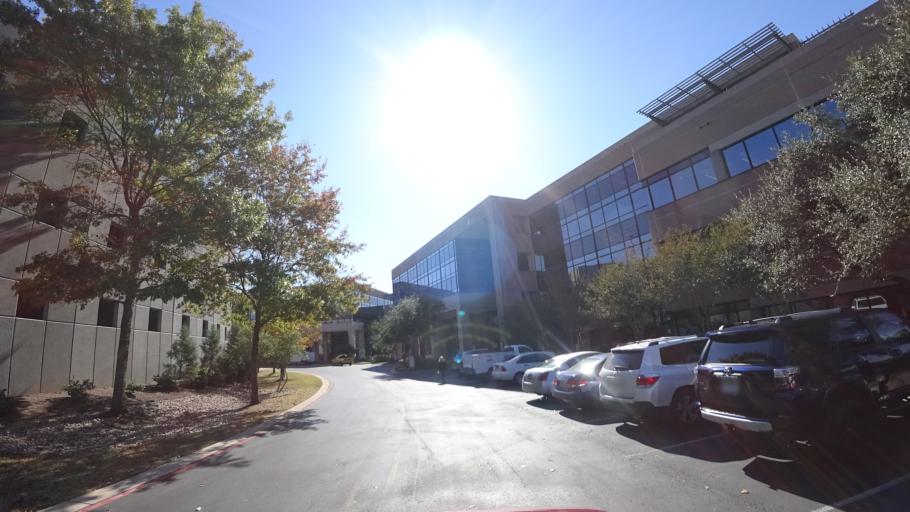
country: US
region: Texas
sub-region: Williamson County
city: Anderson Mill
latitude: 30.3929
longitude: -97.8507
